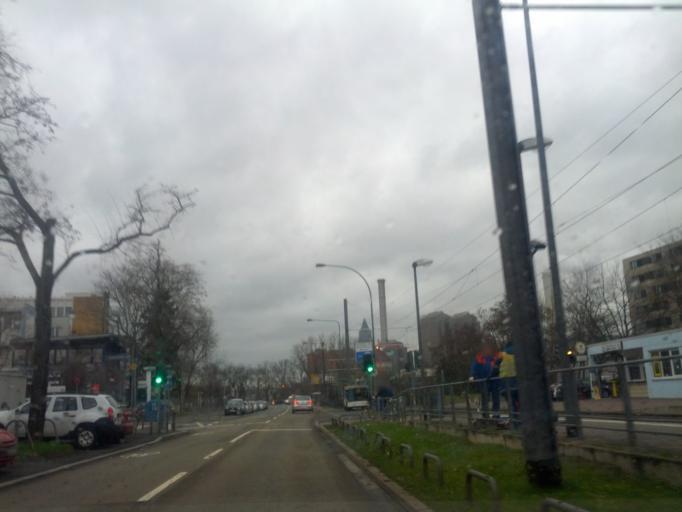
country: DE
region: Hesse
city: Niederrad
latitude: 50.0922
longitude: 8.6529
